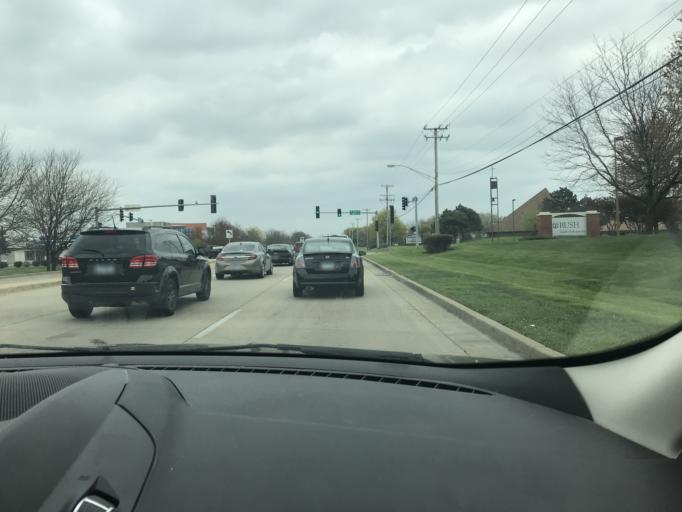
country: US
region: Illinois
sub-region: Kane County
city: Aurora
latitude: 41.7298
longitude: -88.2652
